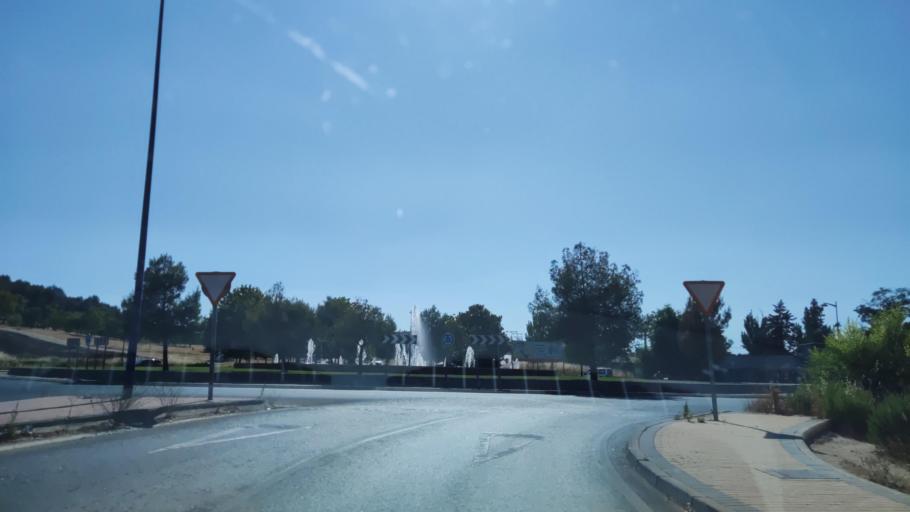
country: ES
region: Madrid
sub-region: Provincia de Madrid
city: Leganes
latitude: 40.3464
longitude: -3.7626
